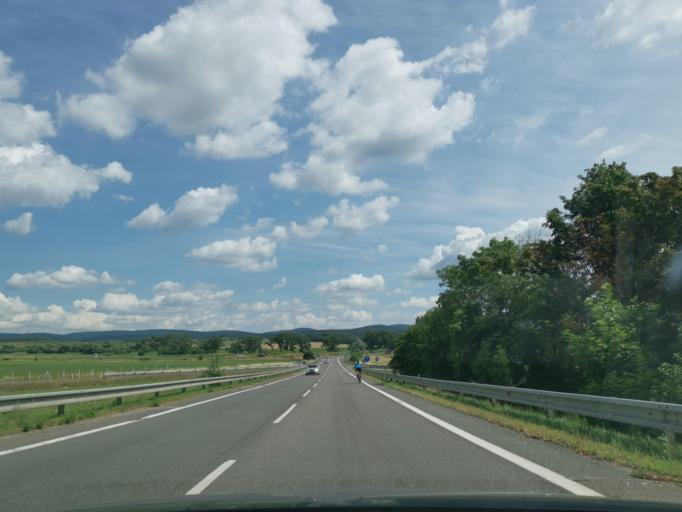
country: SK
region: Bratislavsky
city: Stupava
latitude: 48.3265
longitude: 17.0256
